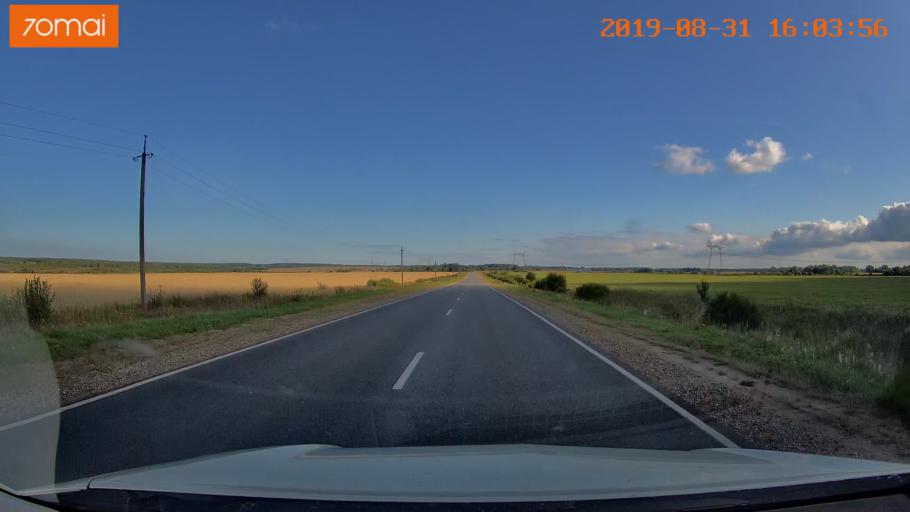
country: RU
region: Kaluga
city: Yukhnov
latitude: 54.6597
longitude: 35.3213
